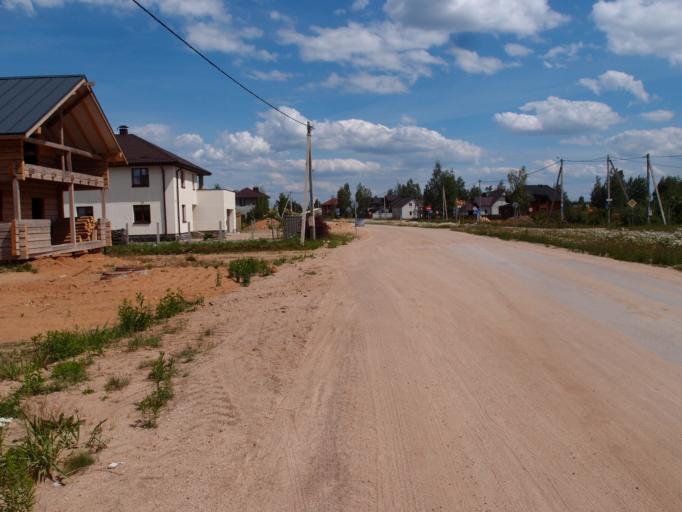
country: BY
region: Minsk
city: Kalodzishchy
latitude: 53.9032
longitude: 27.7969
